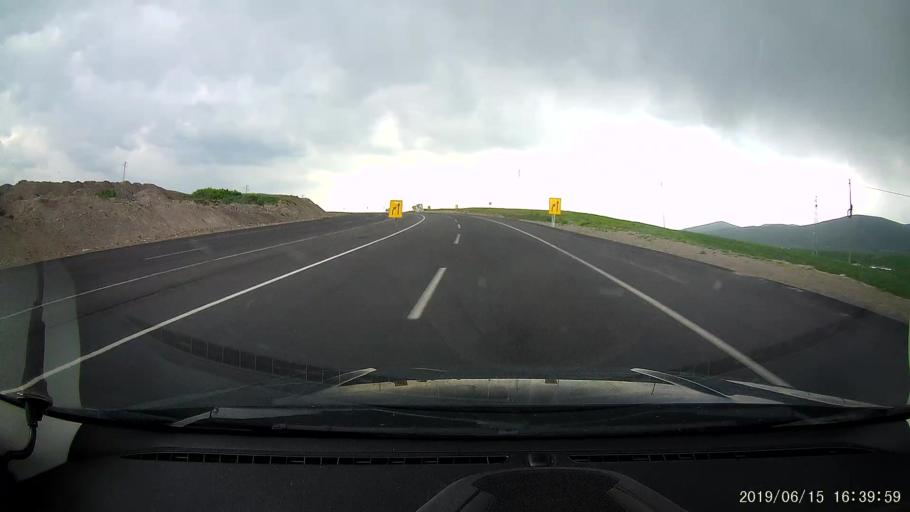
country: TR
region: Ardahan
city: Haskoy
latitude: 40.9753
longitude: 42.8933
